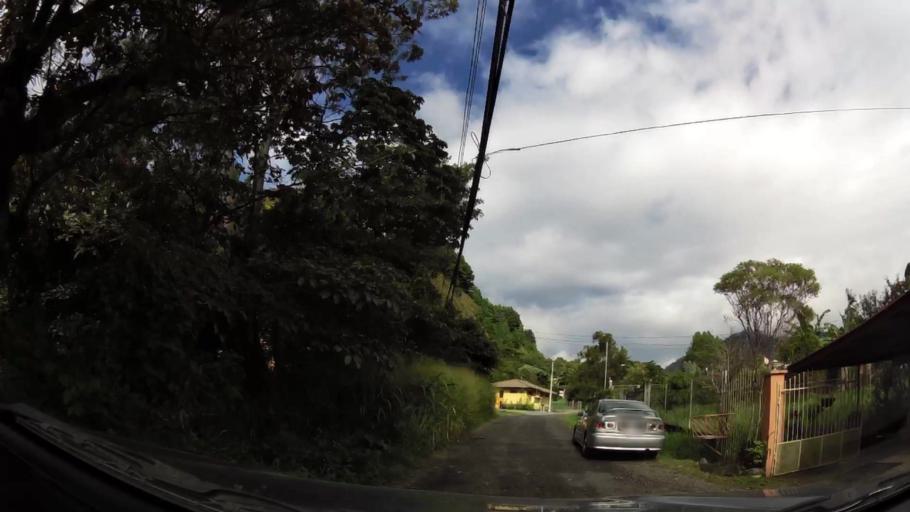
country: PA
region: Chiriqui
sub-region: Distrito Boquete
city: Boquete
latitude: 8.7833
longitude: -82.4333
